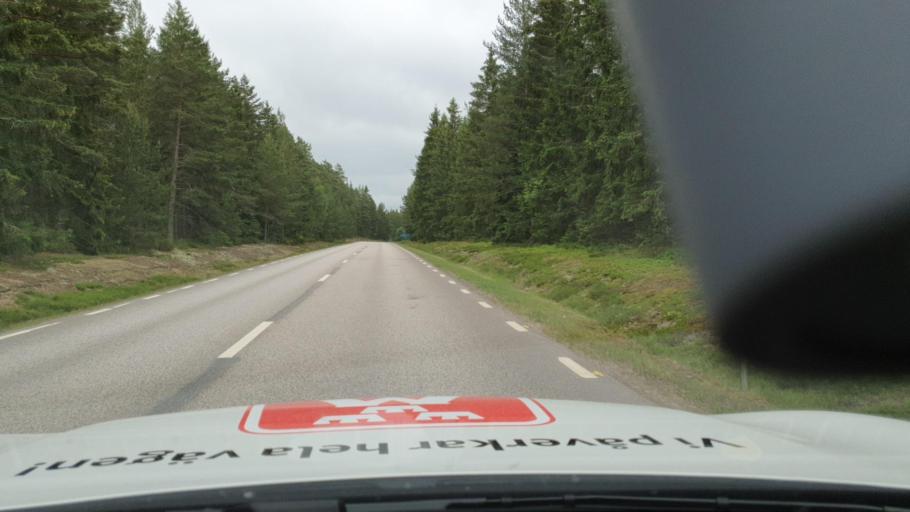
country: SE
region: Vaestra Goetaland
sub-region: Hjo Kommun
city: Hjo
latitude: 58.3456
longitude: 14.2247
